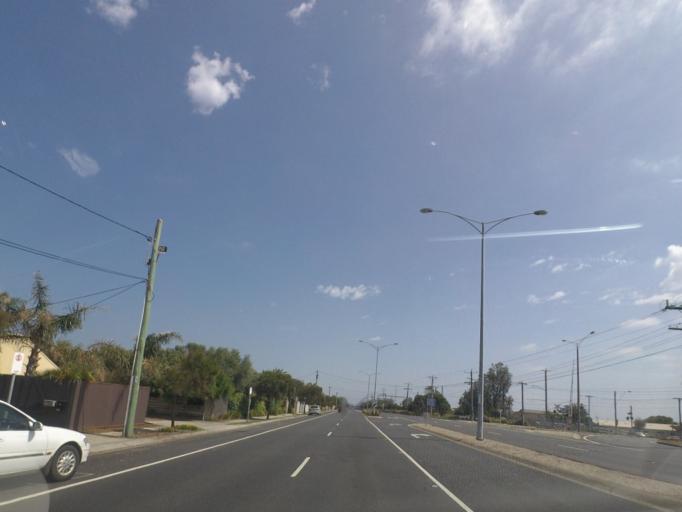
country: AU
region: Victoria
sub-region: Kingston
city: Carrum
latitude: -38.0828
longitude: 145.1240
